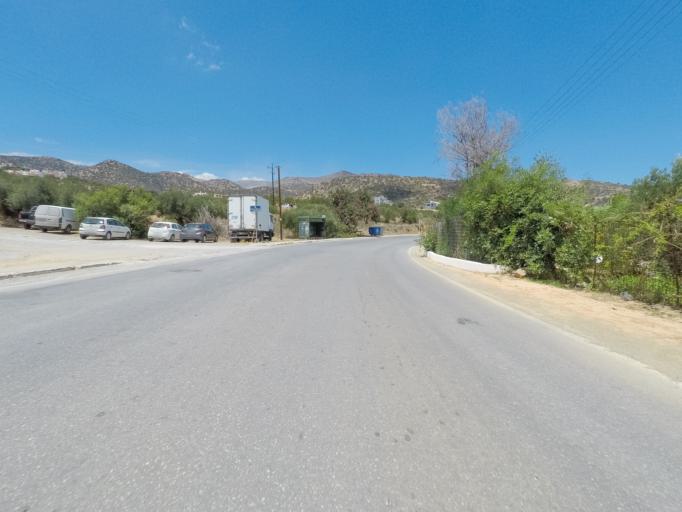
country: GR
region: Crete
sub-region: Nomos Lasithiou
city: Agios Nikolaos
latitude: 35.2142
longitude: 25.7116
